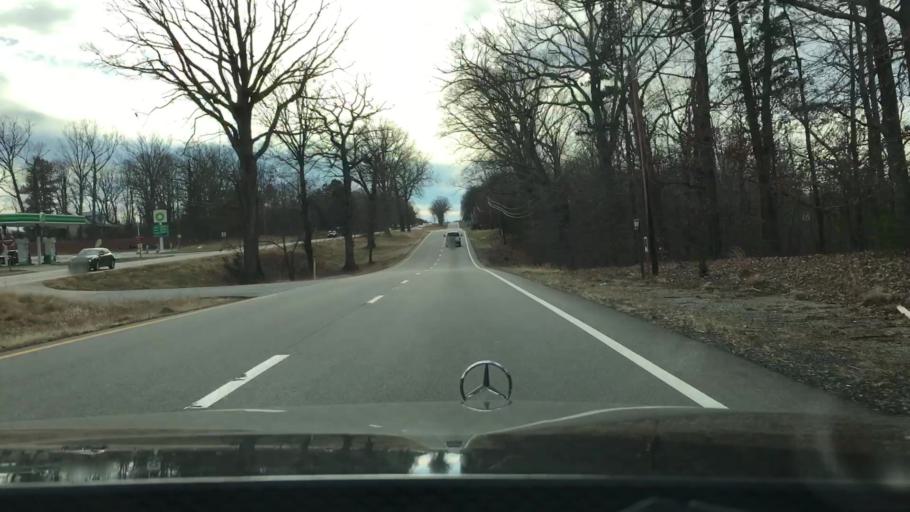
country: US
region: Virginia
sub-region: Pittsylvania County
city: Chatham
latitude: 36.8928
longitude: -79.3995
